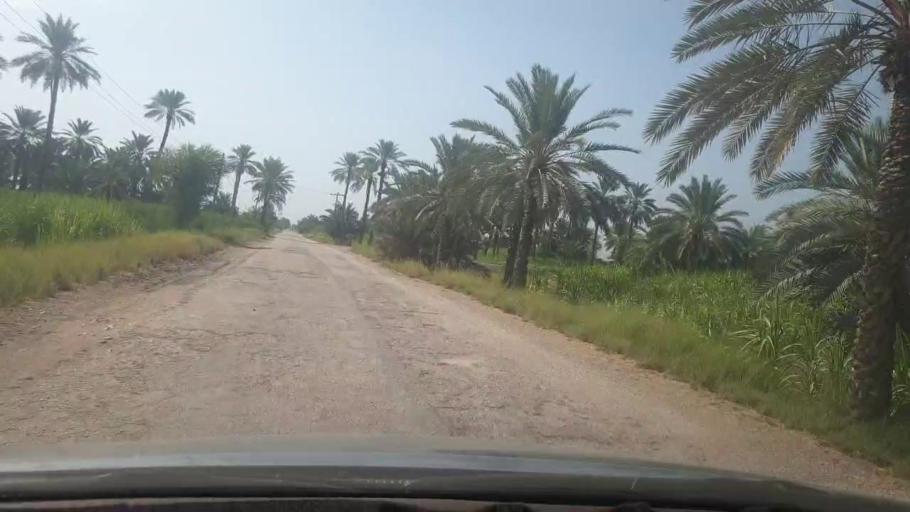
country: PK
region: Sindh
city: Gambat
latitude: 27.3261
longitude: 68.5522
